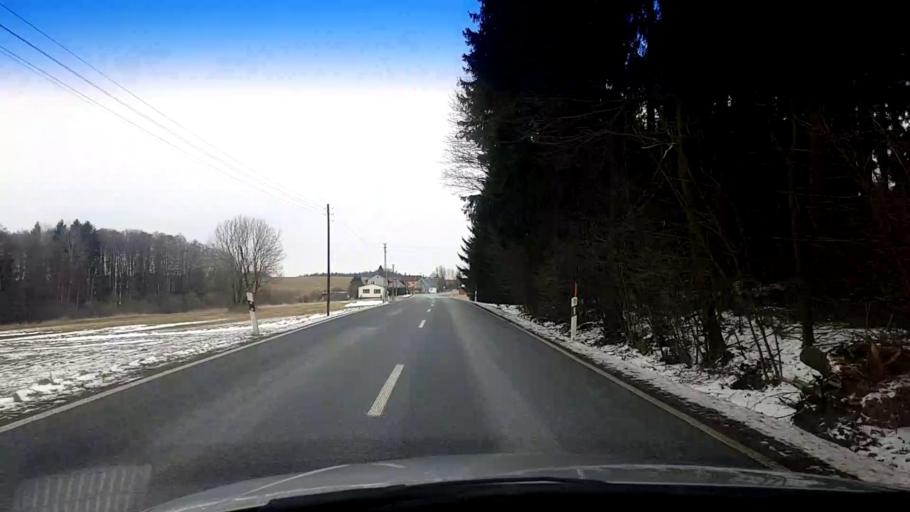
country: DE
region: Bavaria
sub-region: Upper Franconia
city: Stammbach
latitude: 50.1821
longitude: 11.6897
